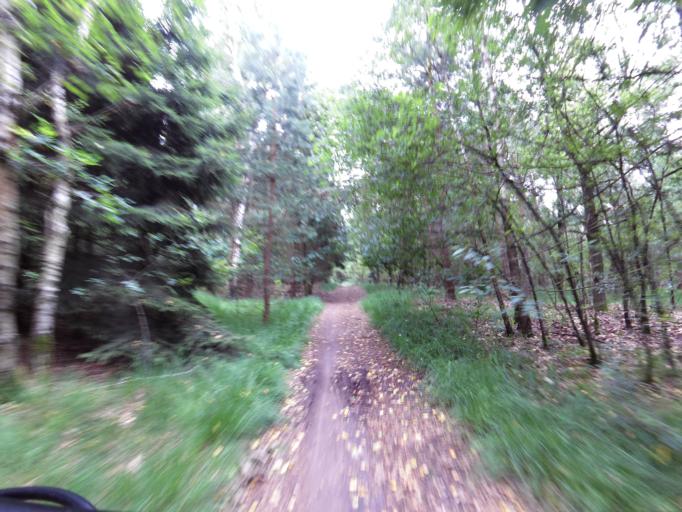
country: NL
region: North Brabant
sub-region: Gemeente Son en Breugel
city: Breugel
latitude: 51.5535
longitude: 5.5191
